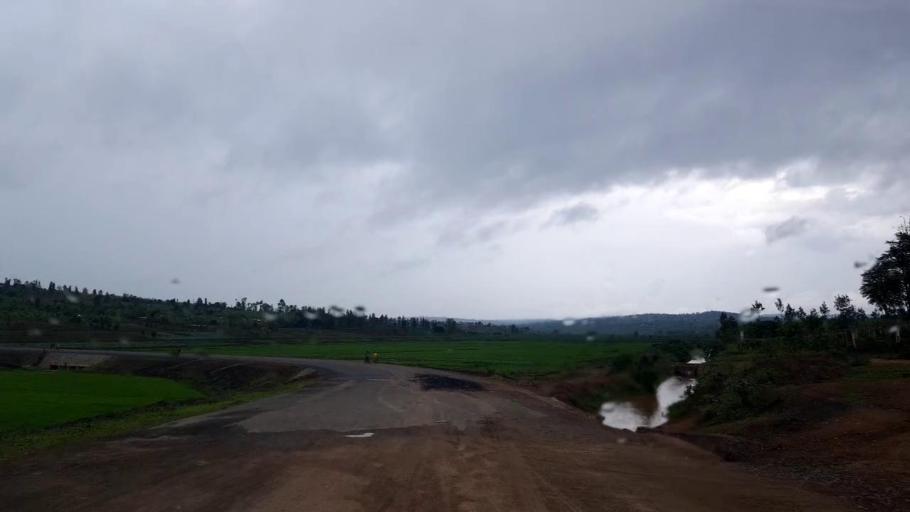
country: RW
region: Northern Province
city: Byumba
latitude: -1.4270
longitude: 30.2728
